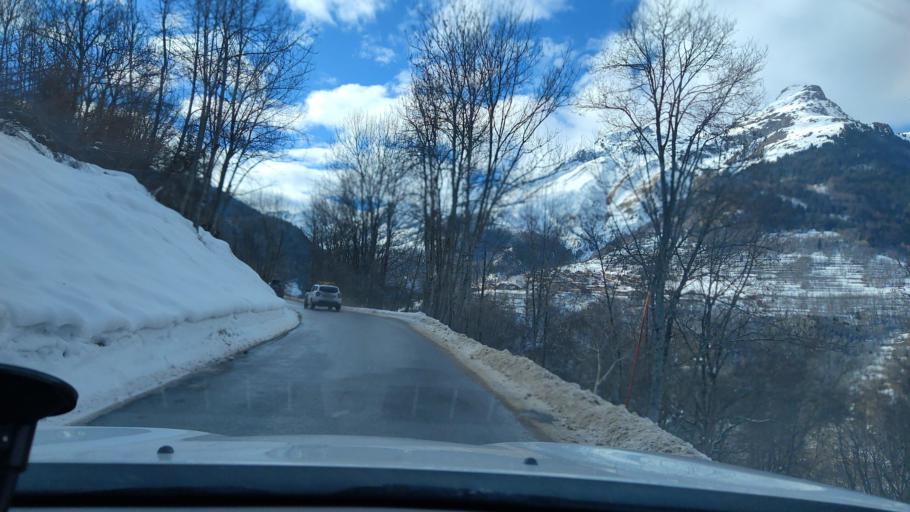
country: FR
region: Rhone-Alpes
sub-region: Departement de la Savoie
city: Saint-Martin-de-Belleville
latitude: 45.4302
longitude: 6.4997
